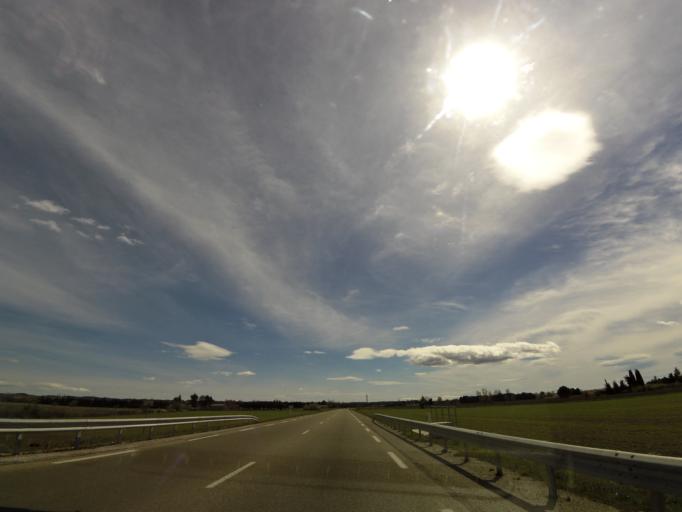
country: FR
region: Languedoc-Roussillon
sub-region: Departement du Gard
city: Bernis
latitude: 43.7635
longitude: 4.2792
